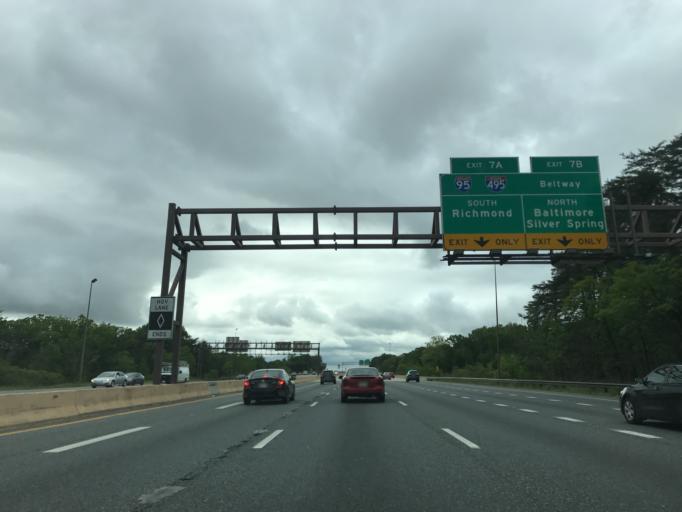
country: US
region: Maryland
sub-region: Prince George's County
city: Springdale
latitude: 38.9469
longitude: -76.8421
